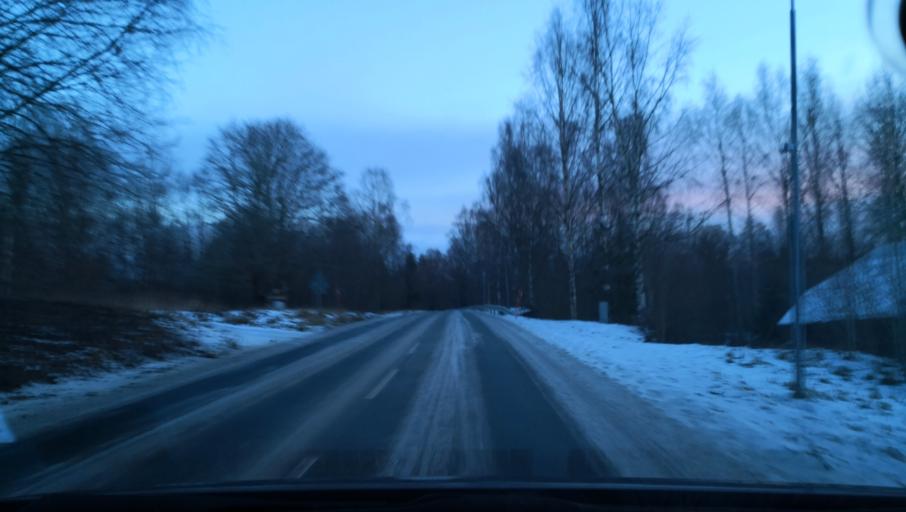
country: SE
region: Soedermanland
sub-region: Katrineholms Kommun
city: Katrineholm
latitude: 59.0875
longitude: 16.2156
